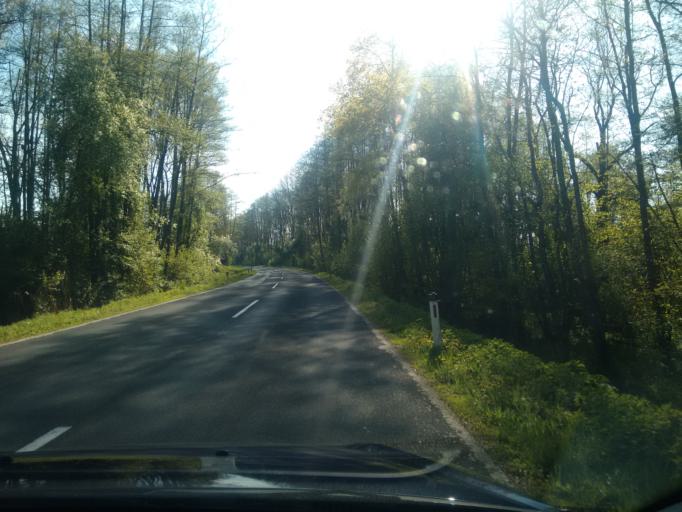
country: AT
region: Upper Austria
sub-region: Wels-Land
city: Buchkirchen
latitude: 48.2204
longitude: 14.0196
